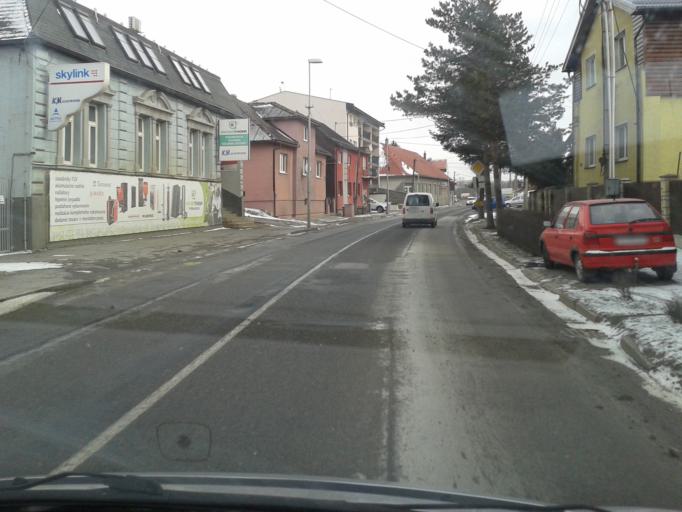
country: SK
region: Zilinsky
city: Tvrdosin
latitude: 49.3370
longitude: 19.5615
